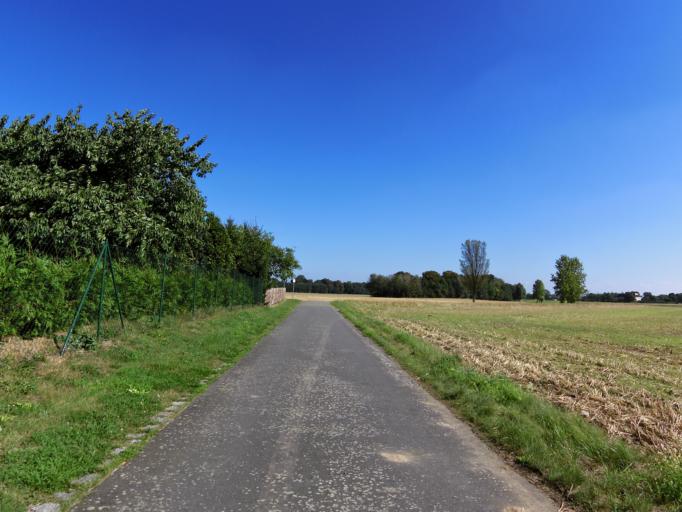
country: DE
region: Saxony
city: Strehla
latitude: 51.3621
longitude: 13.2409
